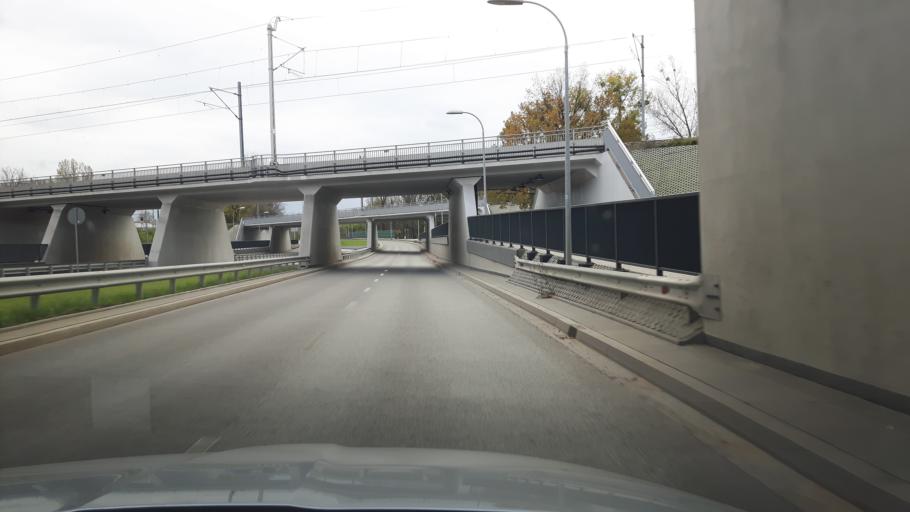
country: PL
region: Masovian Voivodeship
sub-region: Warszawa
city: Praga Poludnie
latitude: 52.2612
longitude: 21.0643
